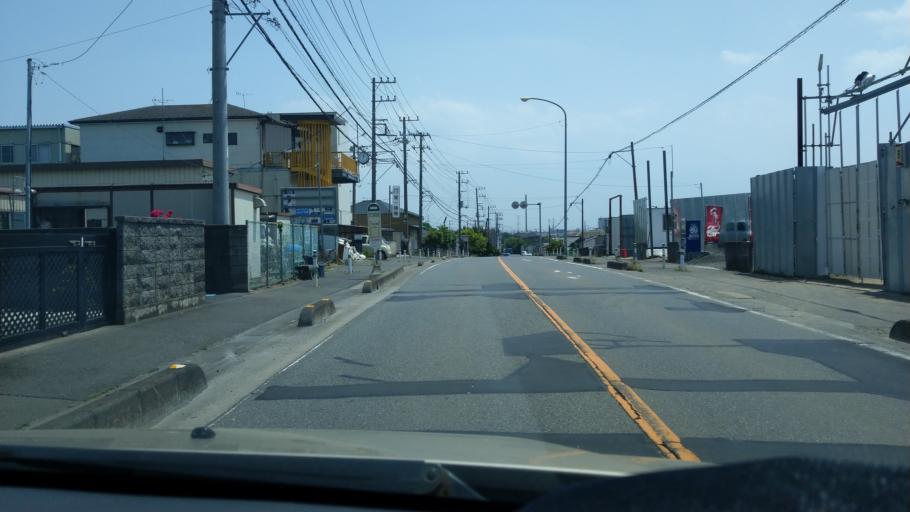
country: JP
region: Saitama
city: Iwatsuki
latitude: 35.9131
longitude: 139.7229
